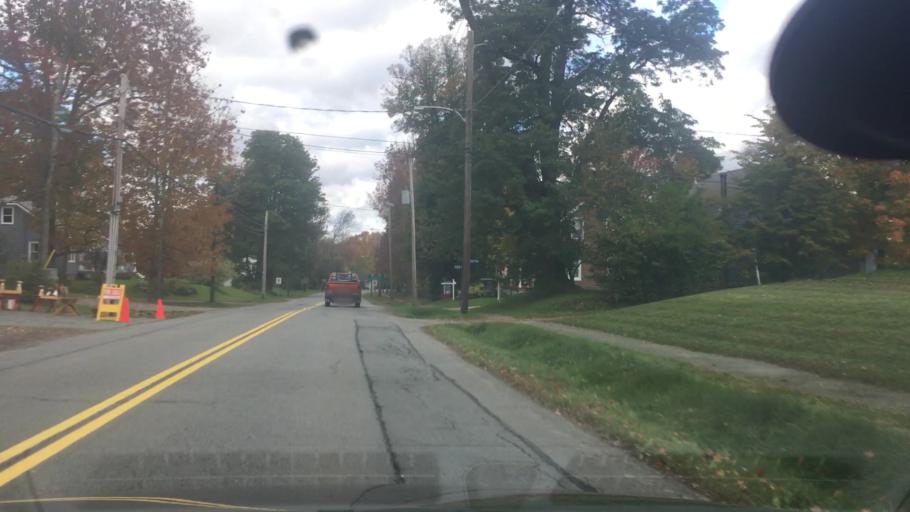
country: CA
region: Nova Scotia
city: Windsor
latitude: 44.9782
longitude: -64.1256
